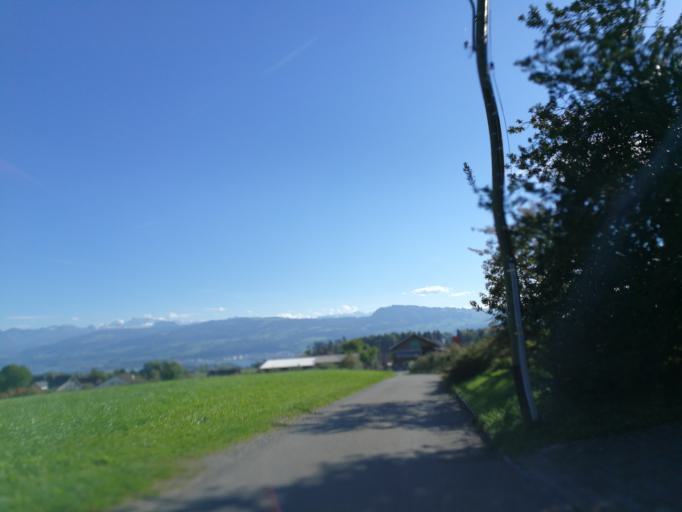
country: CH
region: Zurich
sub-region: Bezirk Meilen
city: Dorf
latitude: 47.2536
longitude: 8.7485
